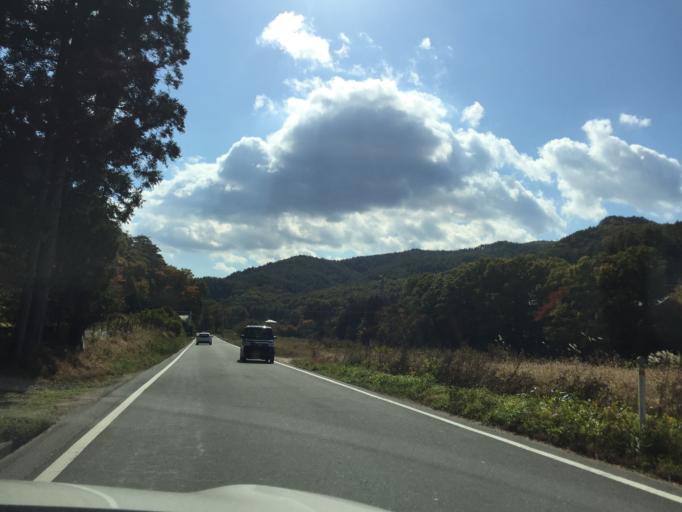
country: JP
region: Fukushima
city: Namie
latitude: 37.3373
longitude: 140.8108
